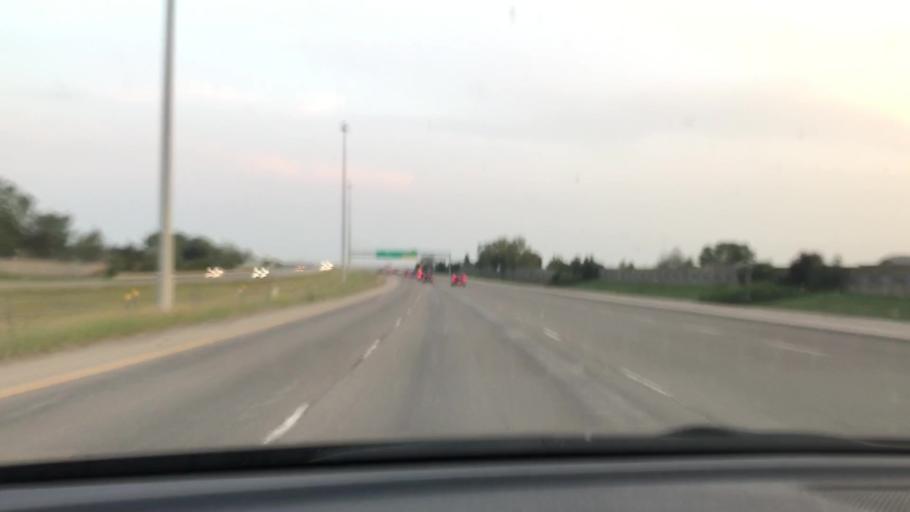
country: CA
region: Alberta
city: Airdrie
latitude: 51.2806
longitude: -114.0021
